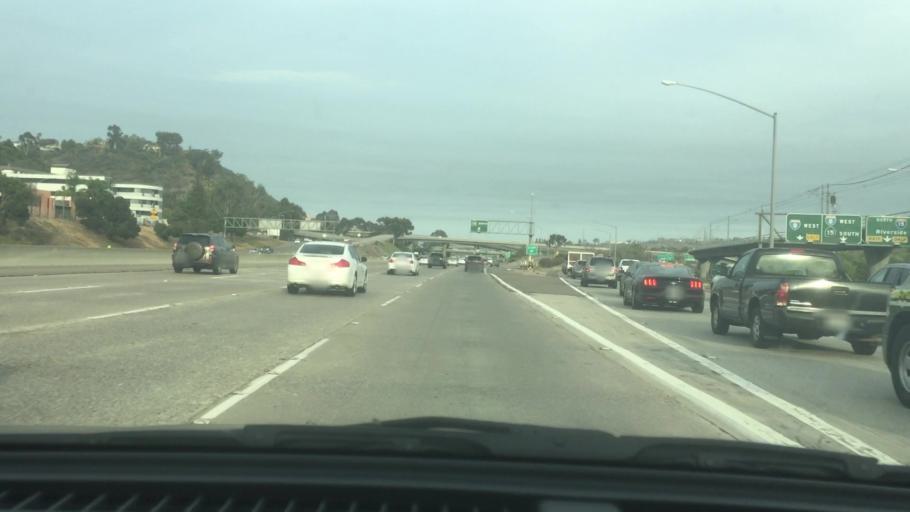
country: US
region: California
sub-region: San Diego County
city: Lemon Grove
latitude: 32.7789
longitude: -117.1046
